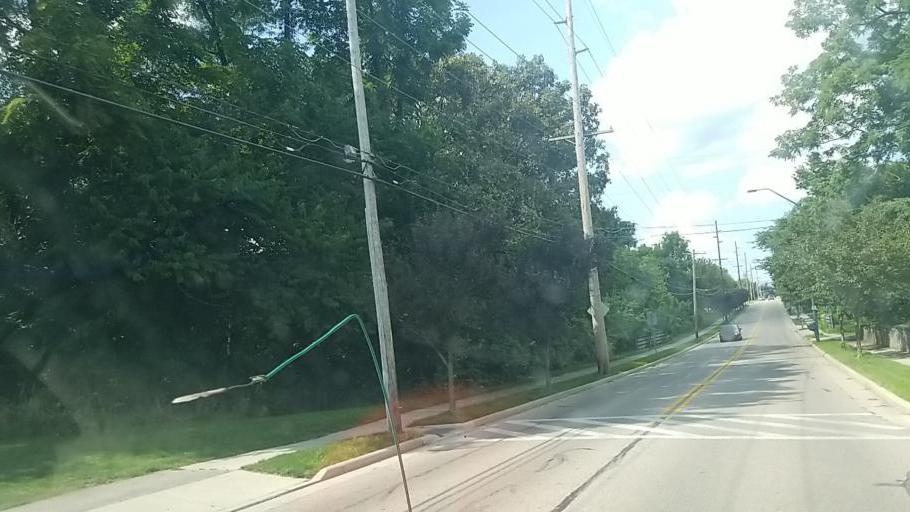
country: US
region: Ohio
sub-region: Franklin County
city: Westerville
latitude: 40.1315
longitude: -82.9402
